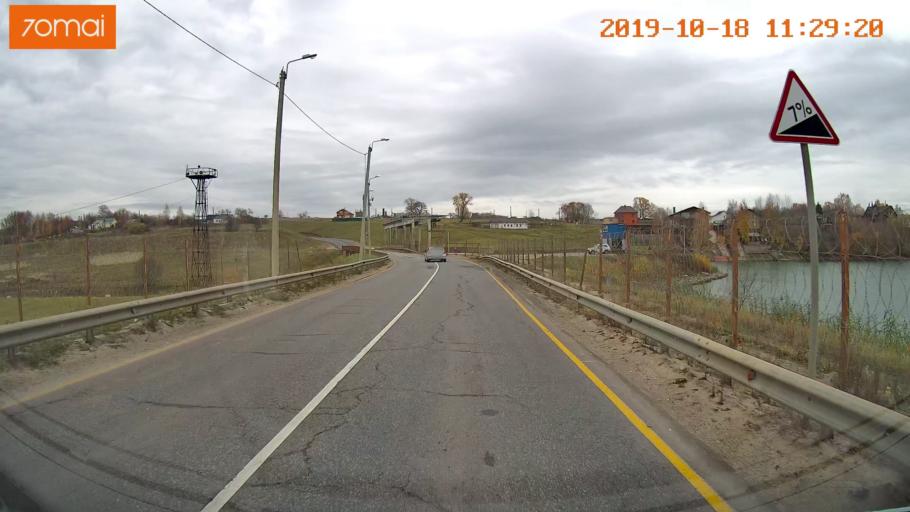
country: RU
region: Rjazan
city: Oktyabr'skiy
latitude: 54.1566
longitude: 38.6760
